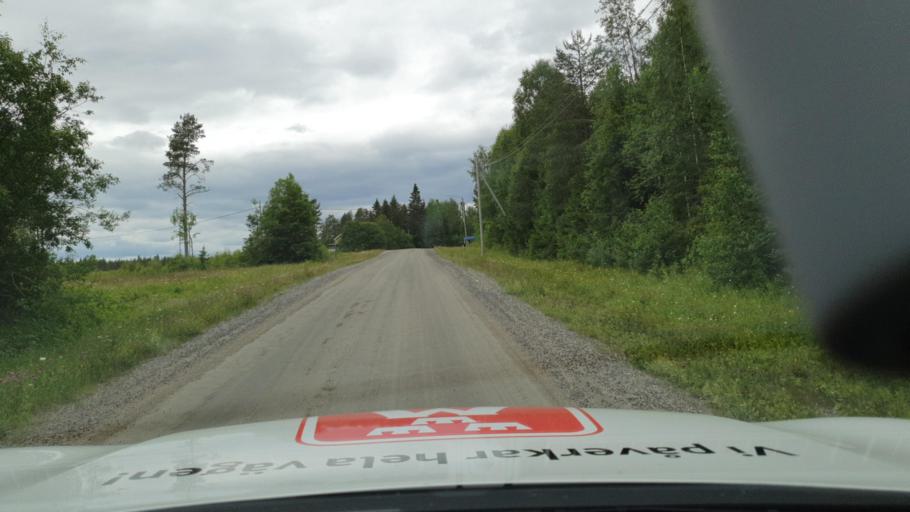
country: SE
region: Vaesterbotten
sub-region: Bjurholms Kommun
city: Bjurholm
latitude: 63.7347
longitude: 19.2953
